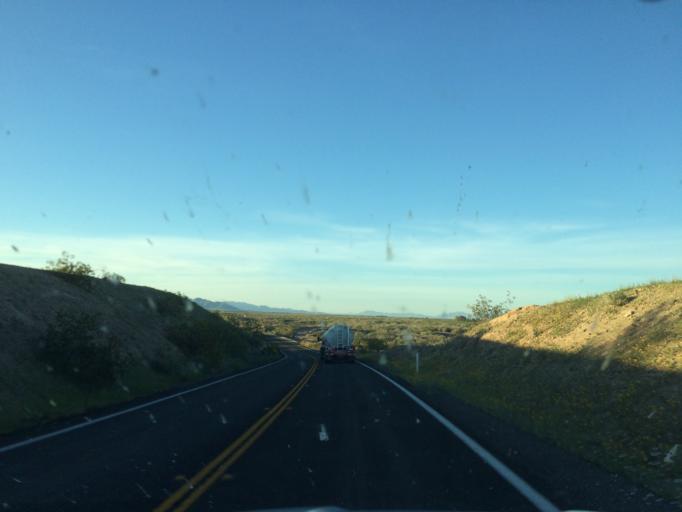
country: US
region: California
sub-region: Riverside County
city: Mesa Verde
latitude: 33.3523
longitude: -114.7224
